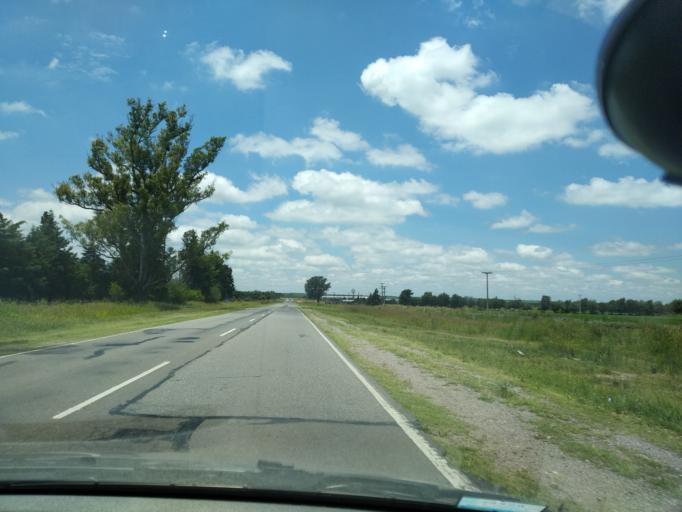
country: AR
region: Cordoba
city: Alta Gracia
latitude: -31.6581
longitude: -64.3712
